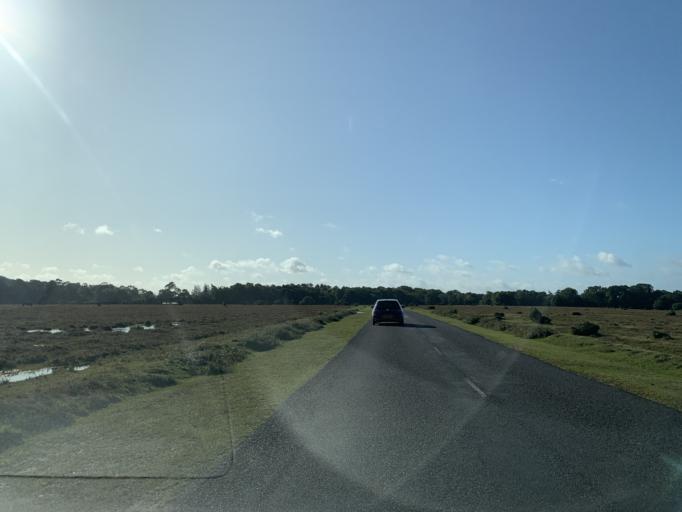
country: GB
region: England
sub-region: Wiltshire
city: Whiteparish
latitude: 50.9362
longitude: -1.6544
